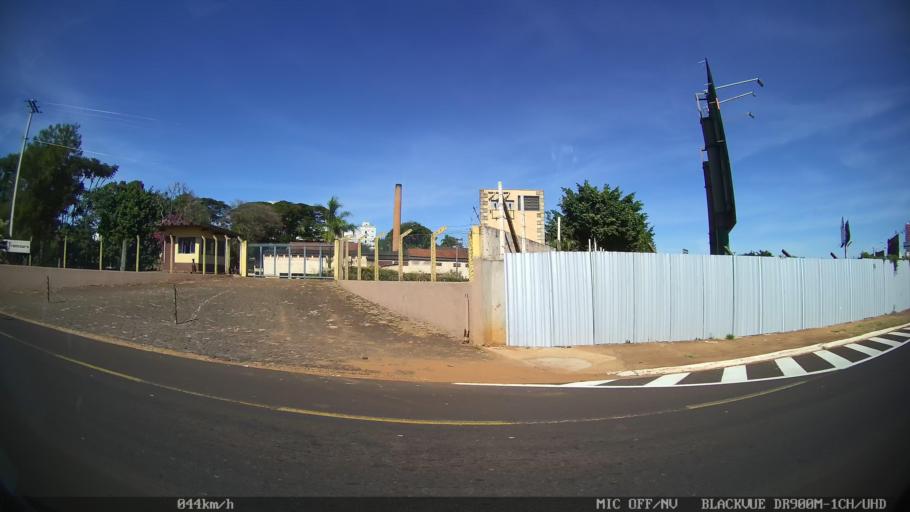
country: BR
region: Sao Paulo
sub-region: Franca
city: Franca
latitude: -20.5524
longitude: -47.4090
